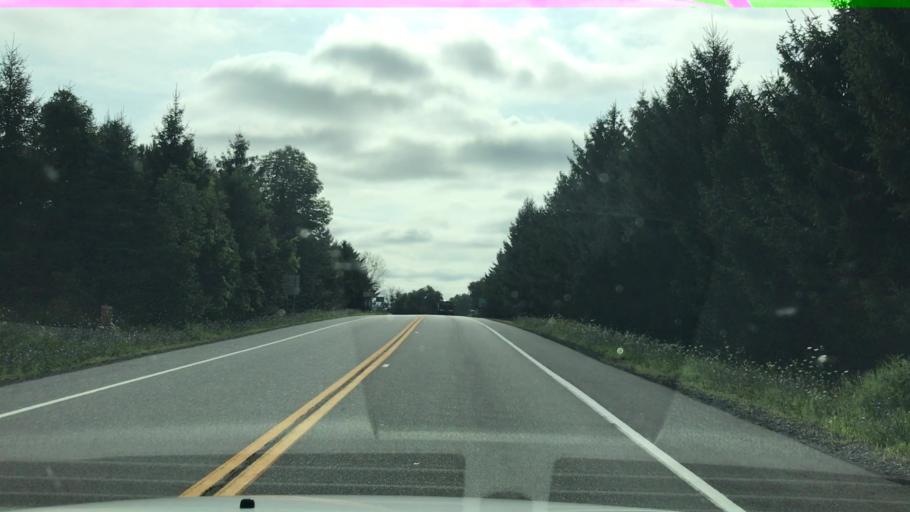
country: US
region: New York
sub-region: Erie County
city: Alden
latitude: 42.8499
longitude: -78.4882
